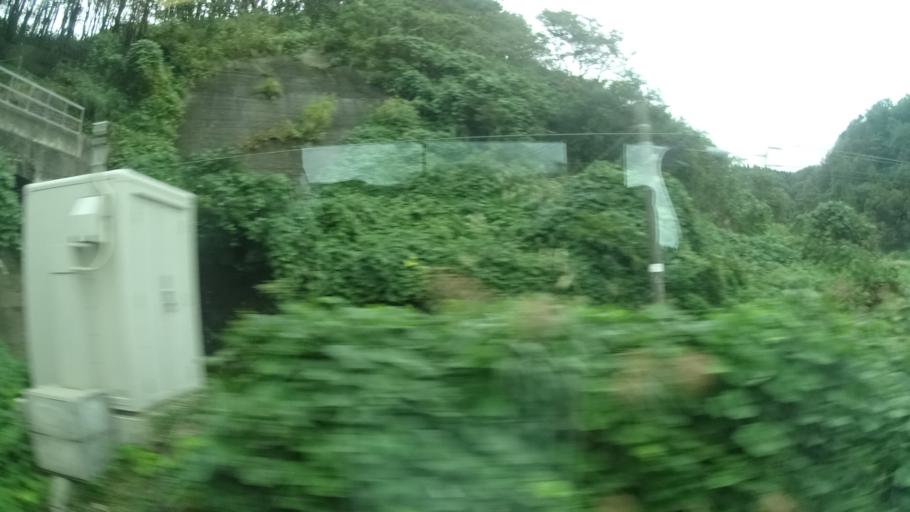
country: JP
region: Yamagata
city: Tsuruoka
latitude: 38.5797
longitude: 139.5599
